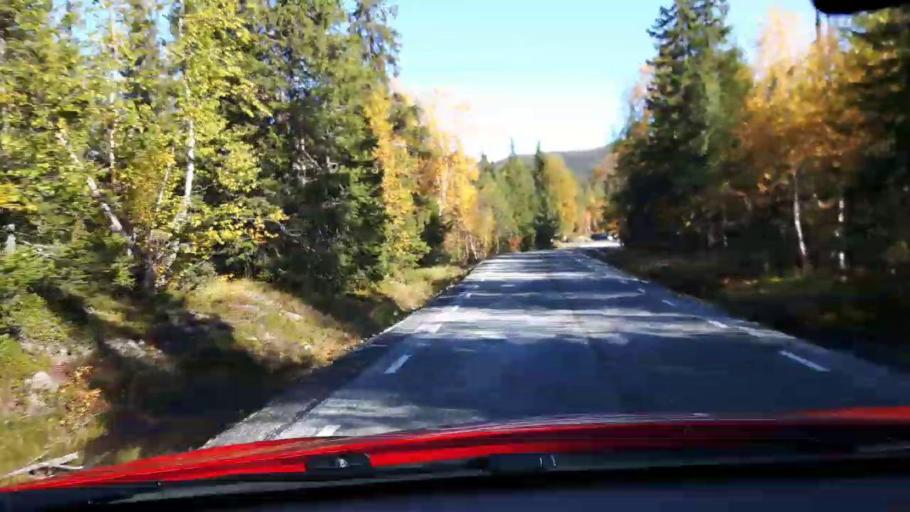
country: NO
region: Nord-Trondelag
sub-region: Royrvik
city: Royrvik
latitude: 64.8184
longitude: 14.2328
